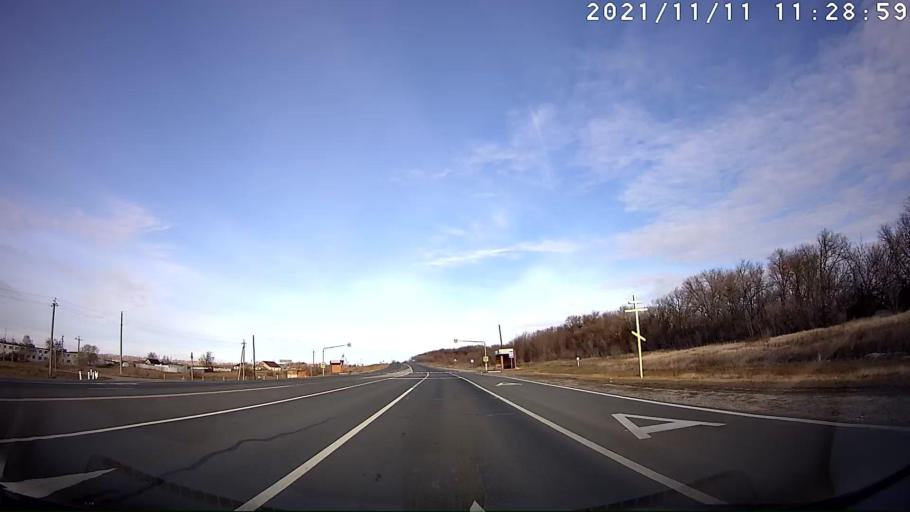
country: RU
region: Samara
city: Varlamovo
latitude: 53.2681
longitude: 48.4804
